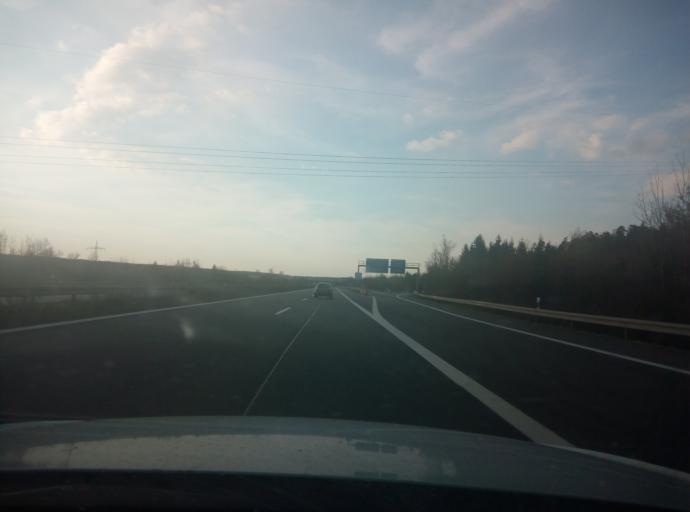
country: DE
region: Baden-Wuerttemberg
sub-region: Freiburg Region
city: Deisslingen
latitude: 48.0872
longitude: 8.5939
